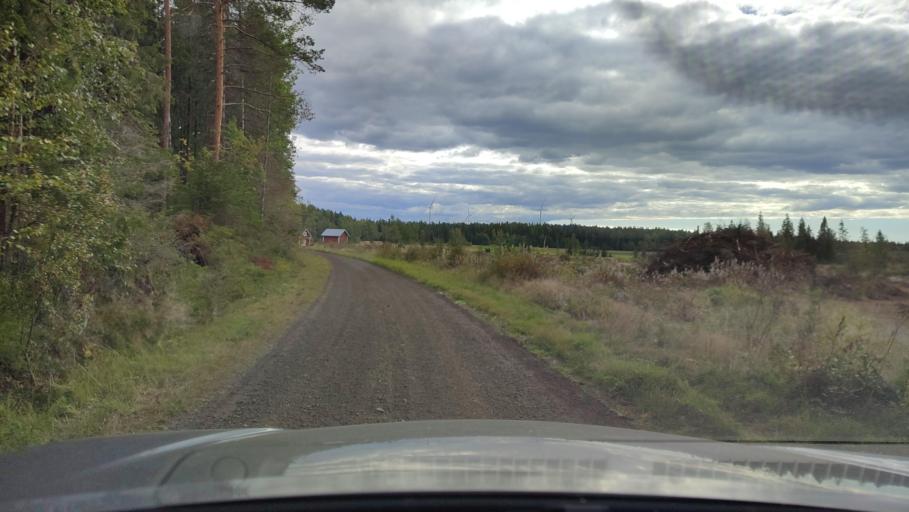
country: FI
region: Southern Ostrobothnia
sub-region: Suupohja
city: Karijoki
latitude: 62.2146
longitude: 21.5668
